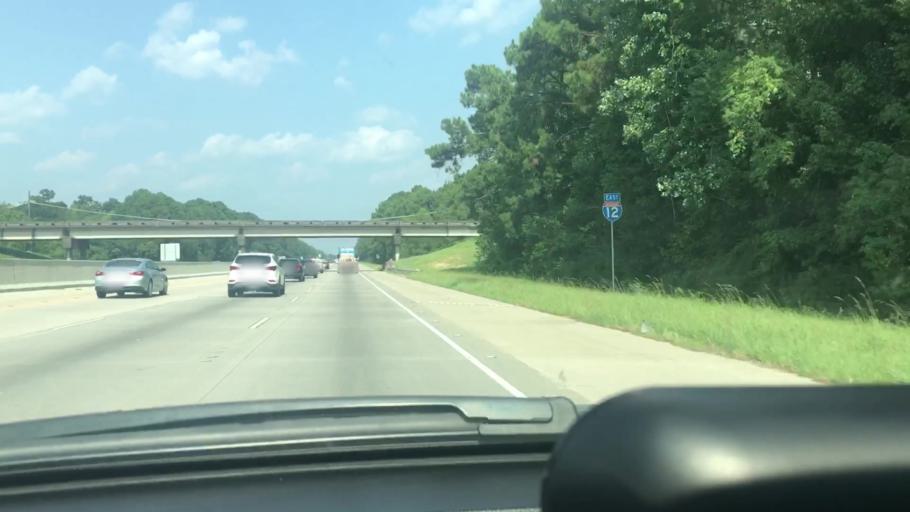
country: US
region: Louisiana
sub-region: Livingston Parish
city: Denham Springs
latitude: 30.4570
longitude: -90.9481
